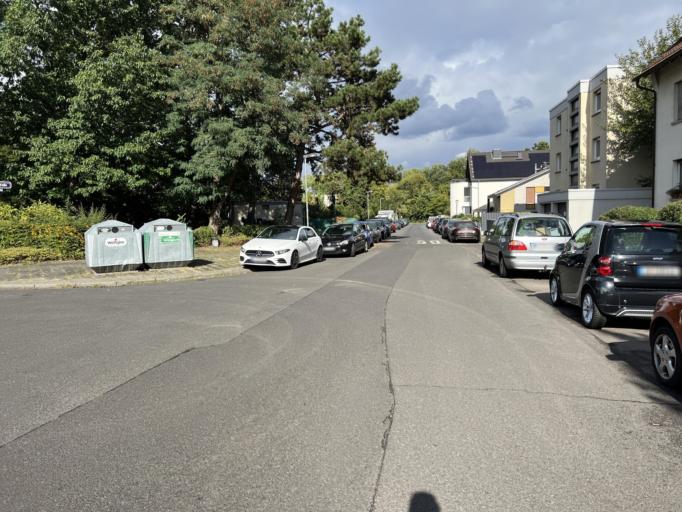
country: DE
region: Hesse
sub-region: Regierungsbezirk Darmstadt
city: Offenbach
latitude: 50.0948
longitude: 8.7499
